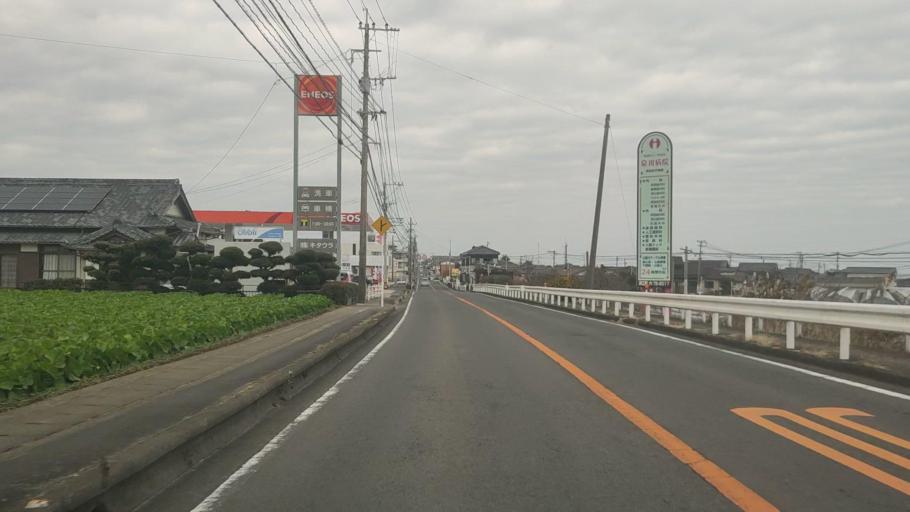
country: JP
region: Nagasaki
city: Shimabara
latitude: 32.8222
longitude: 130.3535
